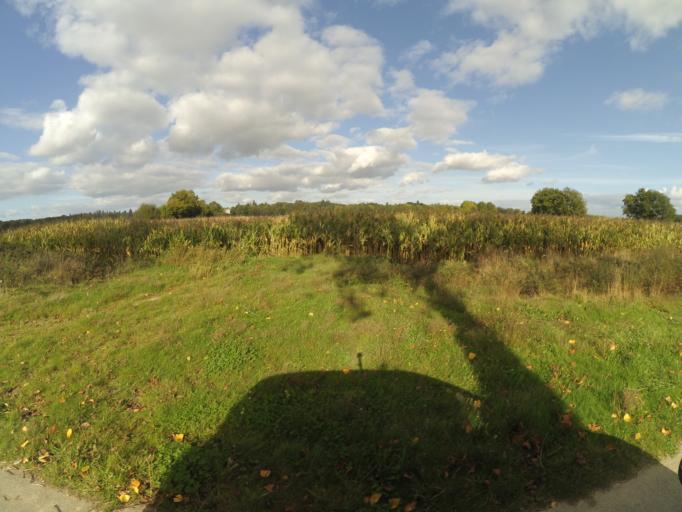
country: FR
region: Brittany
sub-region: Departement du Morbihan
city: Saint-Martin-sur-Oust
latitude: 47.7355
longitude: -2.2362
